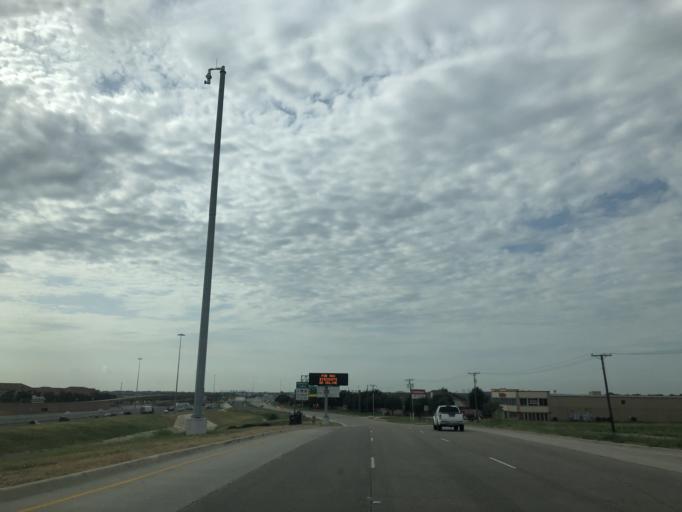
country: US
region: Texas
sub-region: Tarrant County
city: Blue Mound
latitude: 32.8724
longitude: -97.3181
